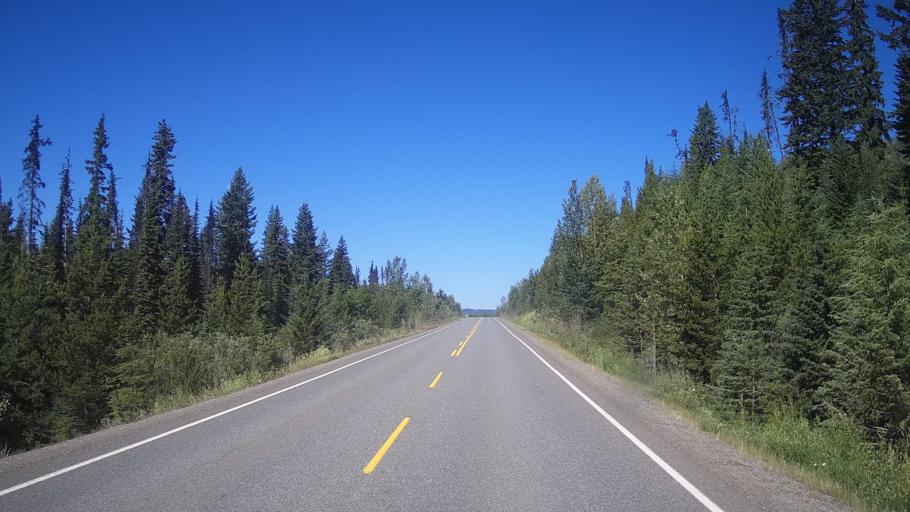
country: CA
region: British Columbia
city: Kamloops
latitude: 51.4963
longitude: -120.3948
